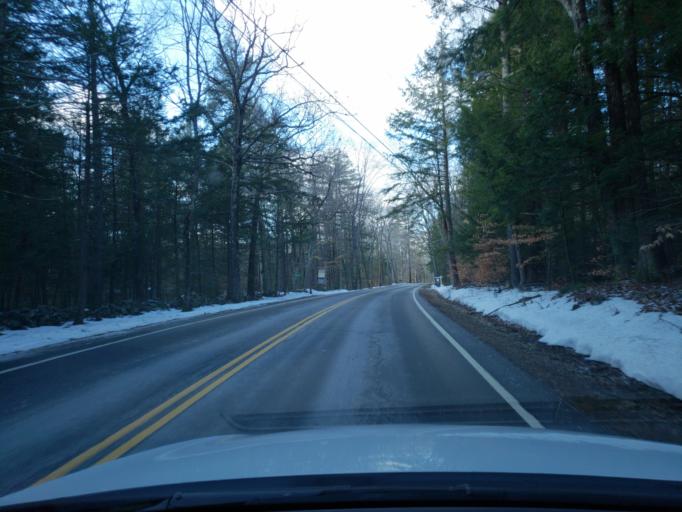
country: US
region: New Hampshire
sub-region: Hillsborough County
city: New Boston
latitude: 42.9915
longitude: -71.7376
